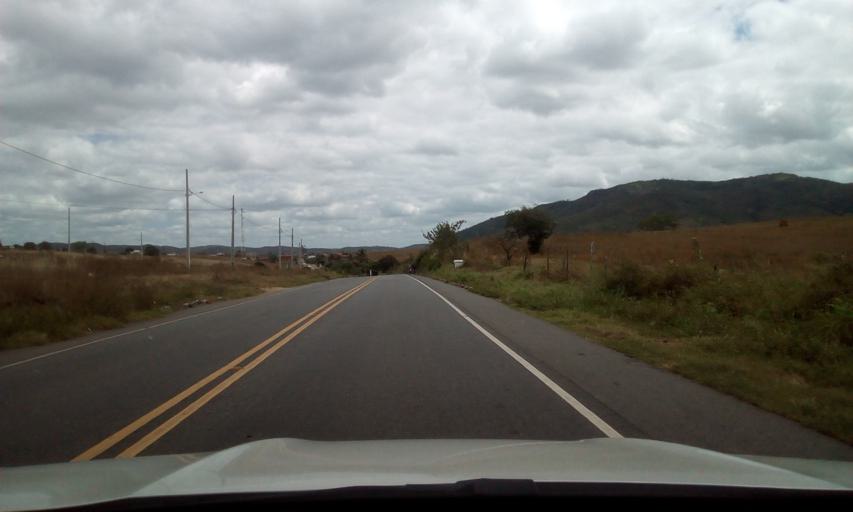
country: BR
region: Paraiba
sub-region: Serra Redonda
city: Alagoa Grande
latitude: -7.1897
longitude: -35.5881
